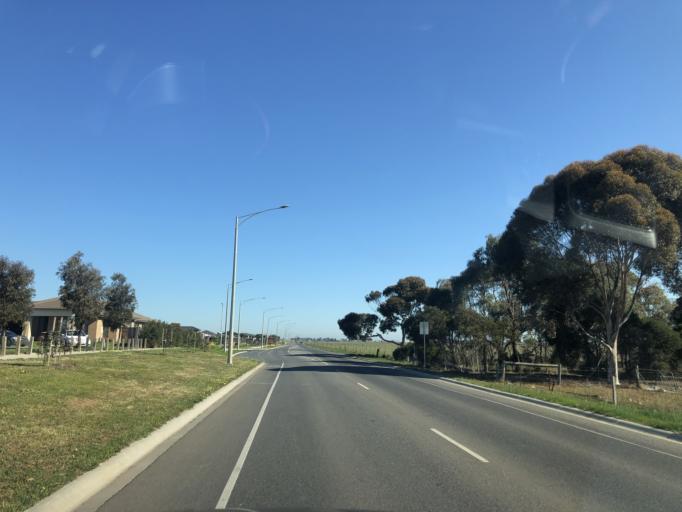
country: AU
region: Victoria
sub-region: Wyndham
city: Hoppers Crossing
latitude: -37.9025
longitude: 144.7158
